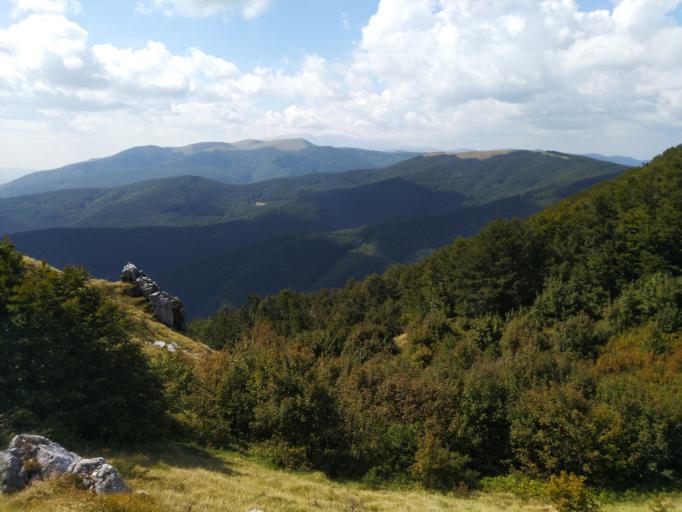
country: BG
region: Stara Zagora
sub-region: Obshtina Kazanluk
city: Shipka
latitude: 42.7471
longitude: 25.3226
